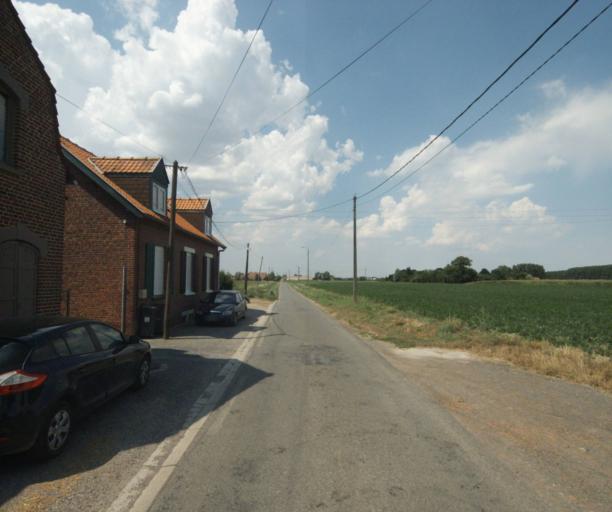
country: FR
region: Nord-Pas-de-Calais
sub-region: Departement du Nord
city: Comines
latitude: 50.7418
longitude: 2.9946
